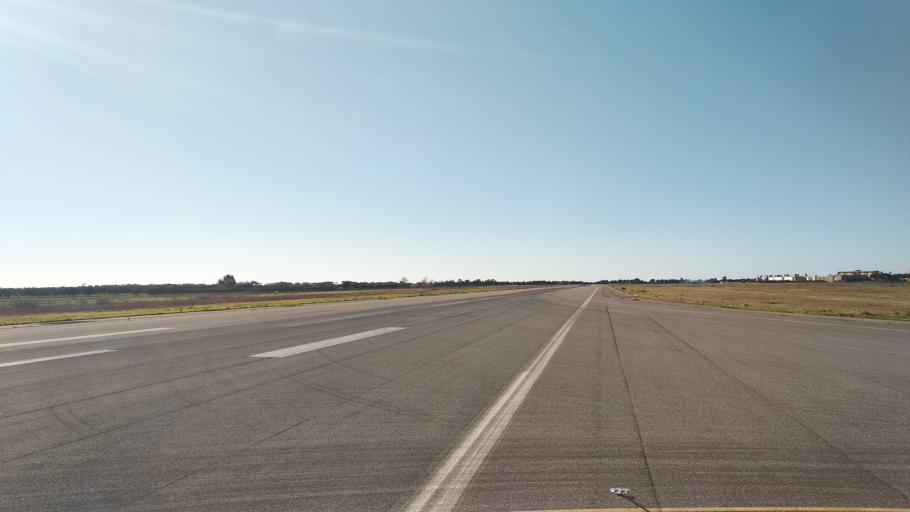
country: IT
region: Calabria
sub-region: Provincia di Catanzaro
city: Santa Eufemia Lamezia
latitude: 38.9049
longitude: 16.2489
